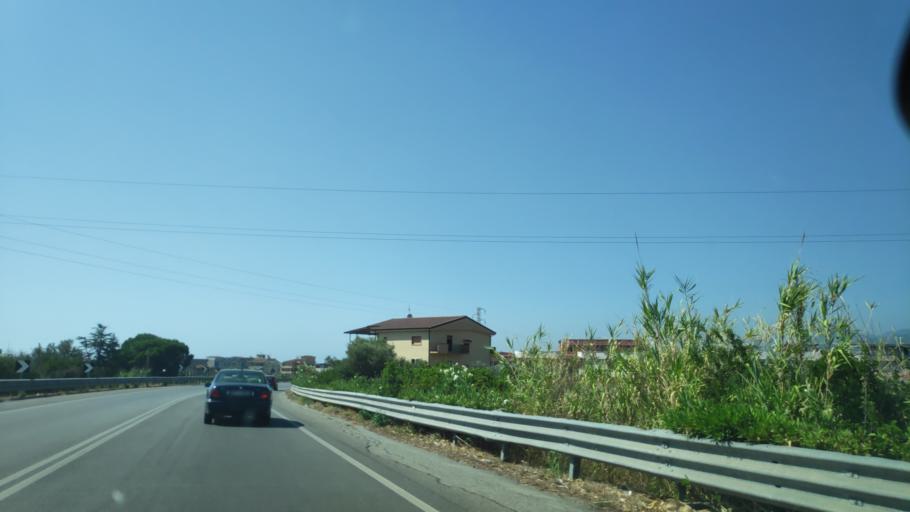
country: IT
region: Calabria
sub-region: Provincia di Reggio Calabria
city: Bovalino
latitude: 38.1459
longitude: 16.1682
